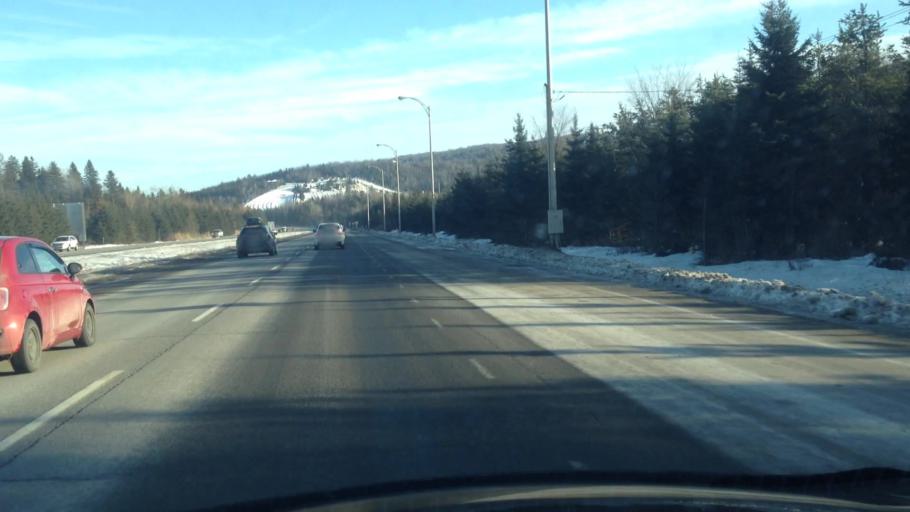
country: CA
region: Quebec
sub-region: Laurentides
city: Saint-Sauveur
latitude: 45.8885
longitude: -74.1389
